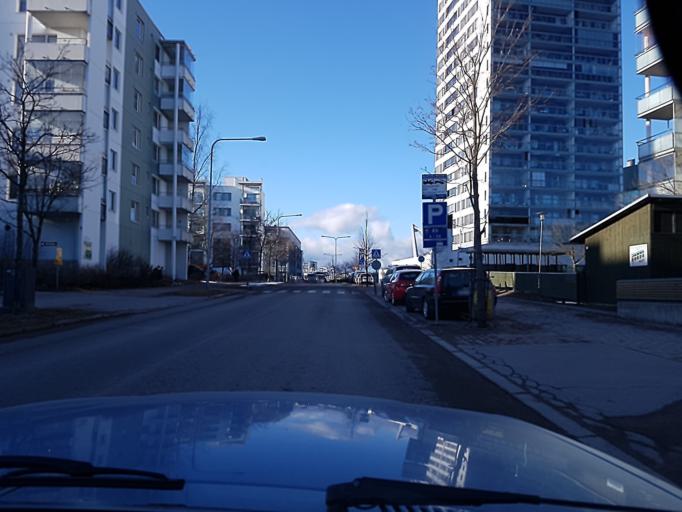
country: FI
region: Uusimaa
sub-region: Helsinki
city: Vantaa
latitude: 60.2051
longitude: 25.1457
